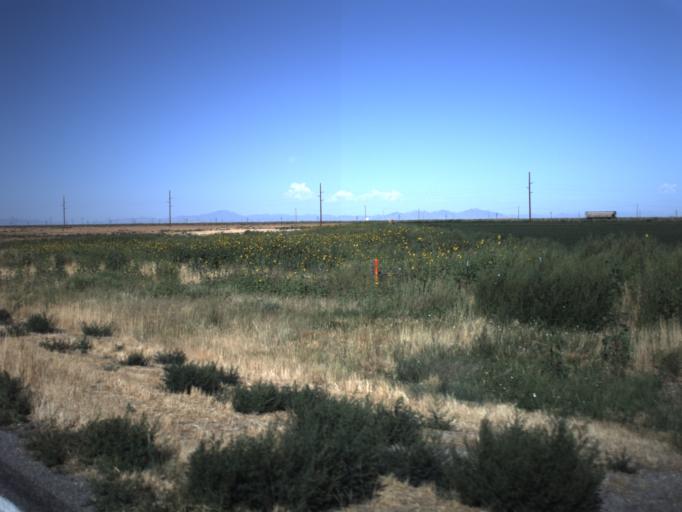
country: US
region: Utah
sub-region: Millard County
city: Delta
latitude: 39.5091
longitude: -112.3814
